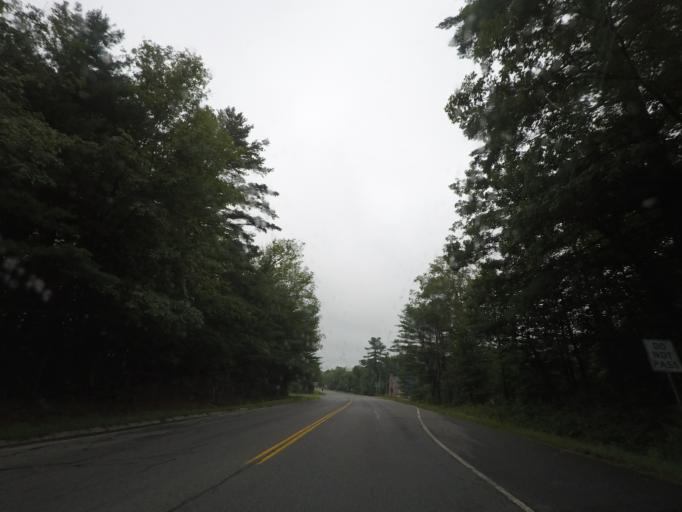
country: US
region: Massachusetts
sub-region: Worcester County
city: Sturbridge
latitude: 42.0922
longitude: -72.0868
